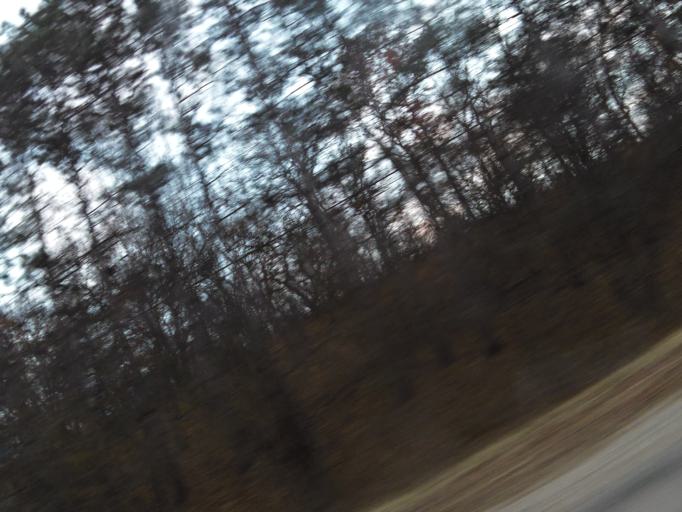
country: US
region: Minnesota
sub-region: Washington County
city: Birchwood
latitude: 45.0503
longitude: -92.9724
